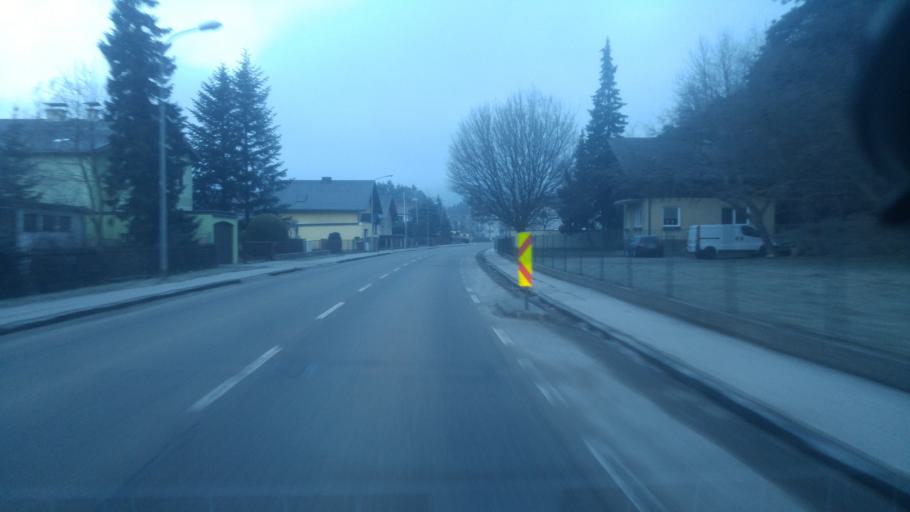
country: AT
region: Lower Austria
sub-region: Politischer Bezirk Baden
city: Pottenstein
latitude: 47.9726
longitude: 16.0728
